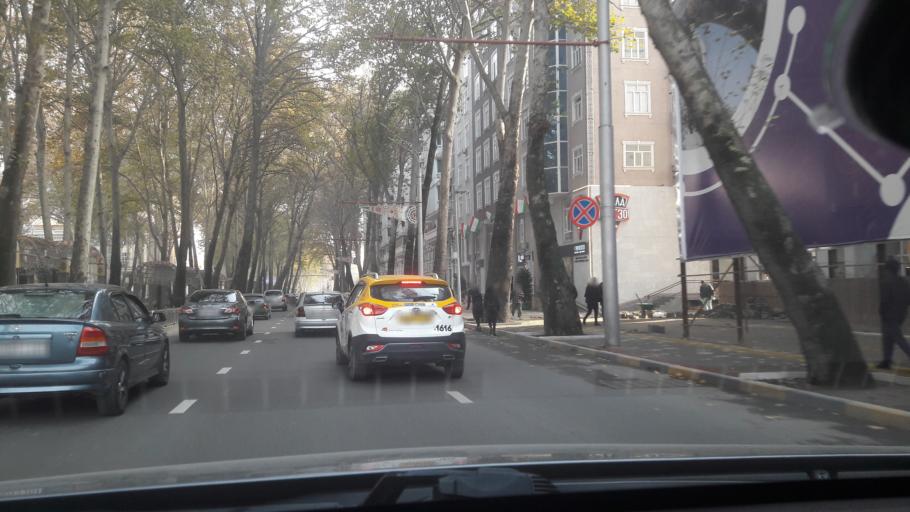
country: TJ
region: Dushanbe
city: Dushanbe
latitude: 38.5733
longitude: 68.7874
